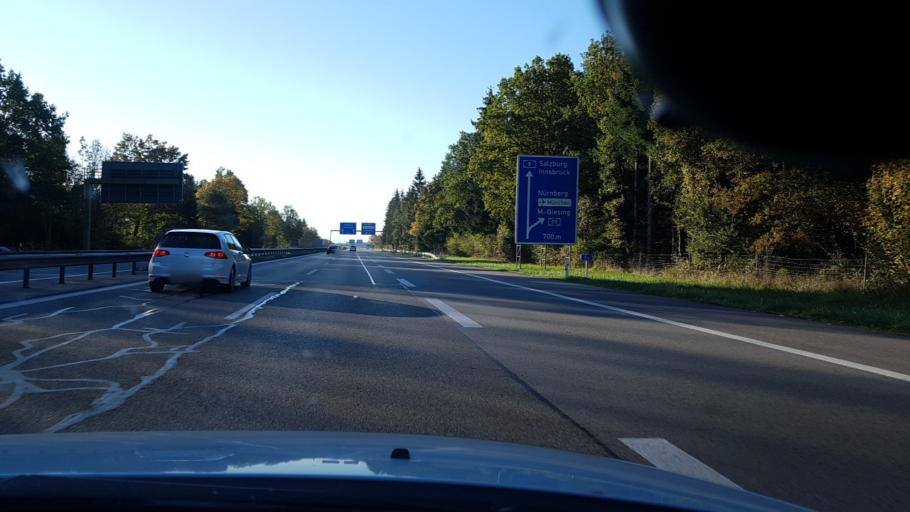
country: DE
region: Bavaria
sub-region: Upper Bavaria
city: Ottobrunn
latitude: 48.0391
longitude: 11.6515
